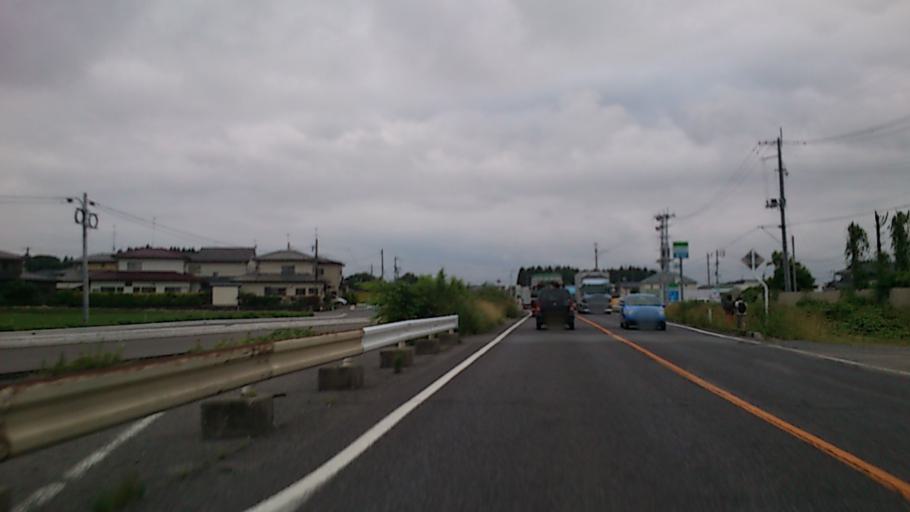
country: JP
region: Fukushima
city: Sukagawa
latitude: 37.2505
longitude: 140.3396
